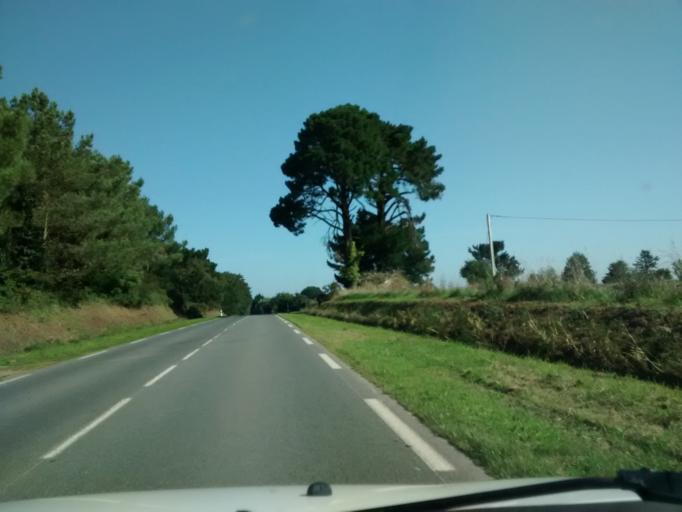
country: FR
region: Brittany
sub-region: Departement des Cotes-d'Armor
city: Tredarzec
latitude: 48.8046
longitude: -3.1992
